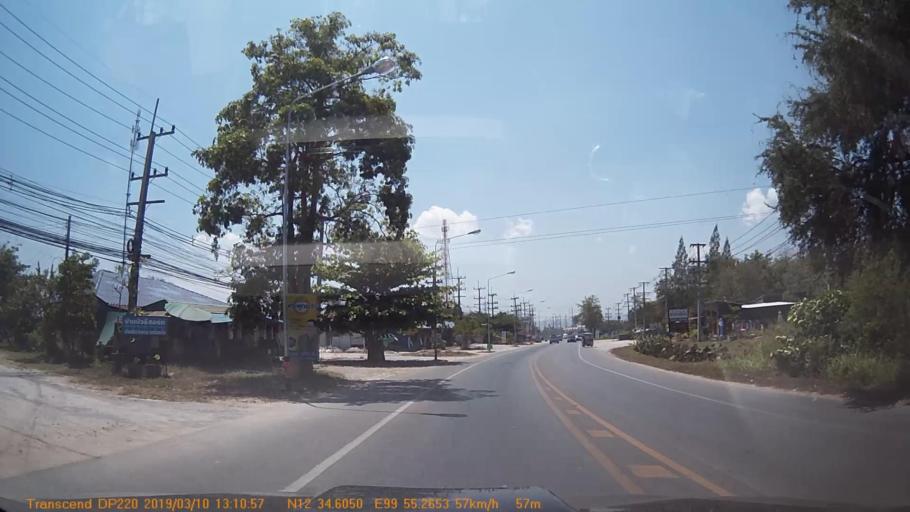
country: TH
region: Prachuap Khiri Khan
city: Hua Hin
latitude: 12.5767
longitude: 99.9209
